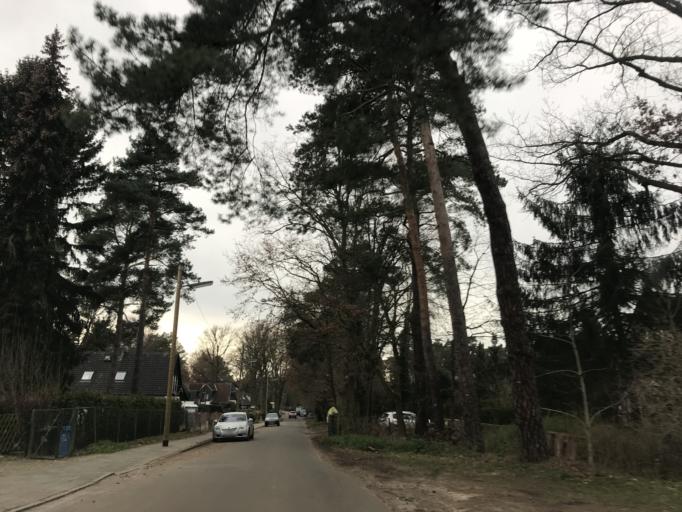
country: DE
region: Berlin
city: Kladow
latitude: 52.4536
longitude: 13.1185
